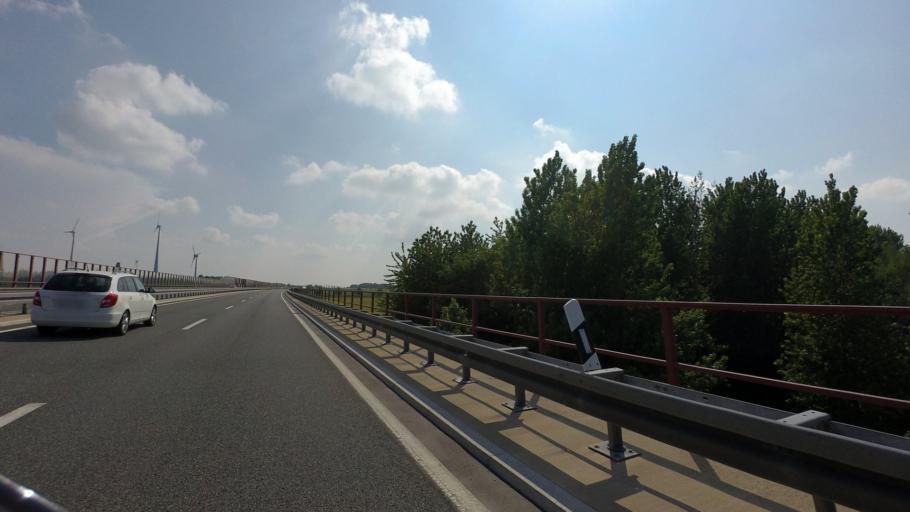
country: DE
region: Saxony
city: Lobau
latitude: 51.1390
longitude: 14.6533
